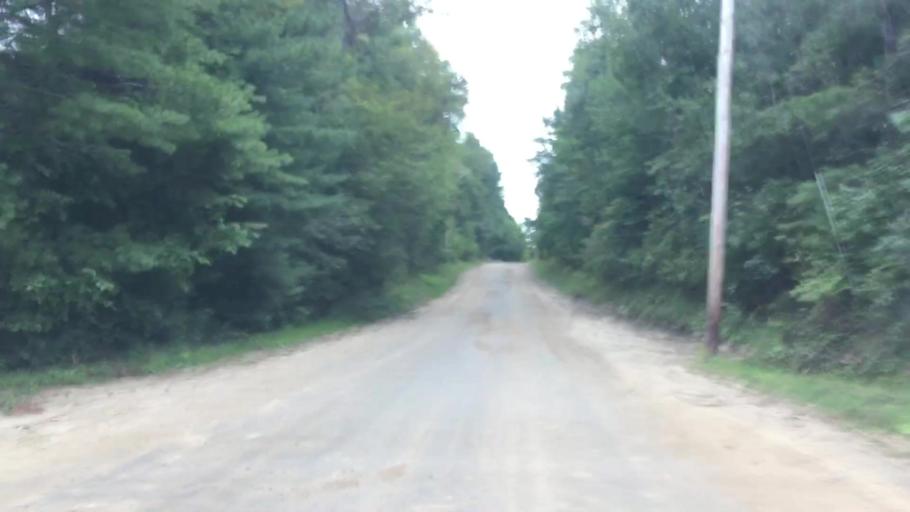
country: US
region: Maine
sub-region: Cumberland County
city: New Gloucester
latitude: 43.9068
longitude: -70.2354
